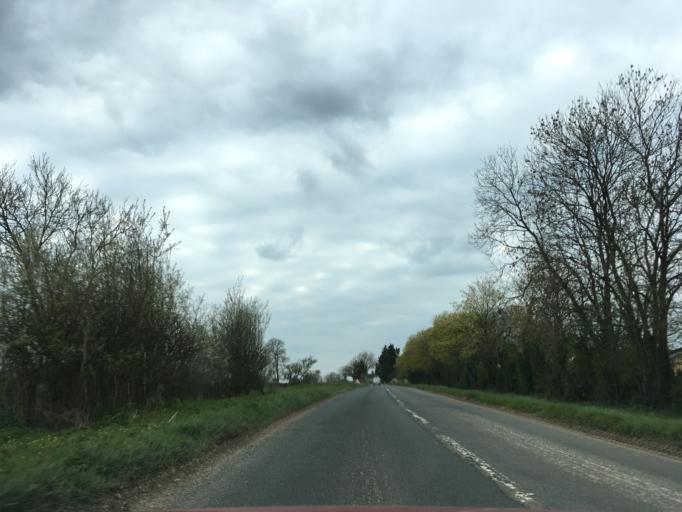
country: GB
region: England
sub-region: Gloucestershire
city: Northleach
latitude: 51.7667
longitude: -1.8203
